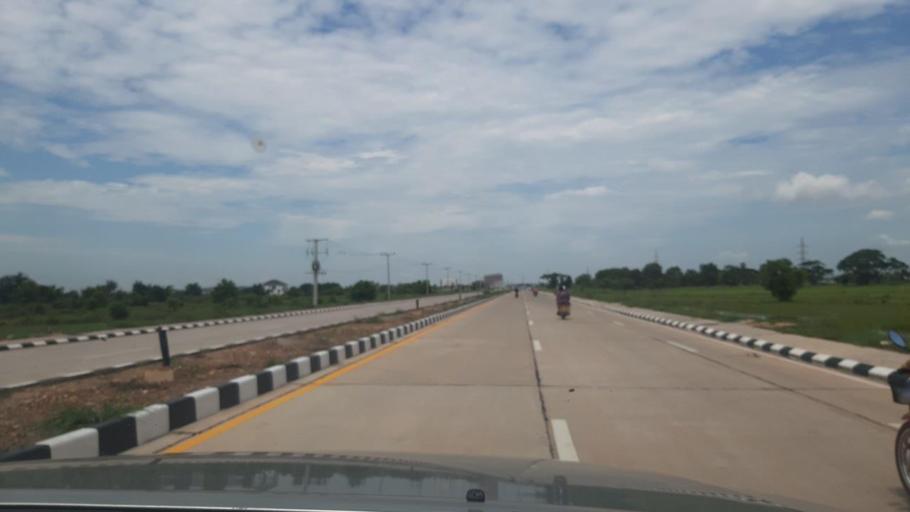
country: LA
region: Vientiane
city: Vientiane
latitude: 18.0214
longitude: 102.5957
